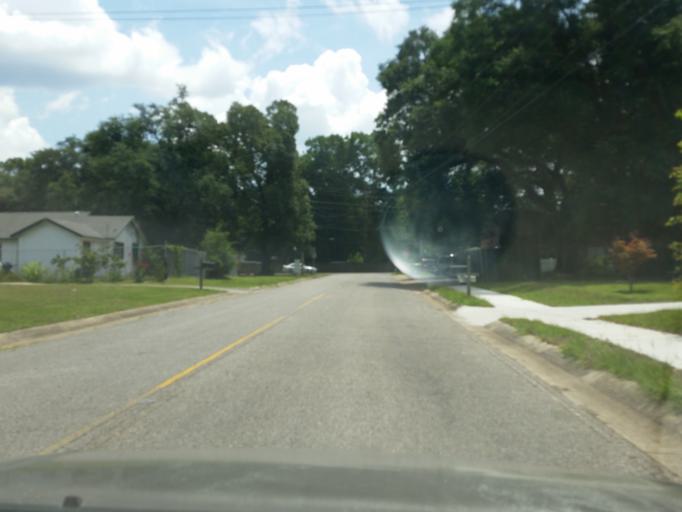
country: US
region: Florida
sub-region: Escambia County
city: Ferry Pass
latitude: 30.5108
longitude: -87.1956
